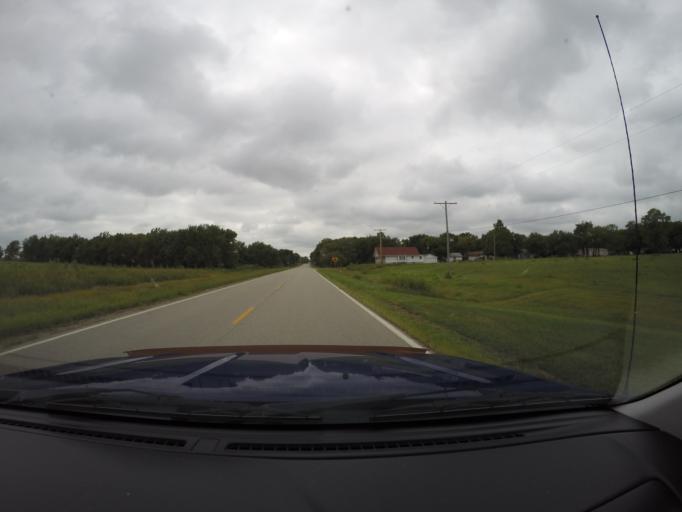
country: US
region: Kansas
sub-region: Morris County
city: Council Grove
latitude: 38.8412
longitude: -96.5887
